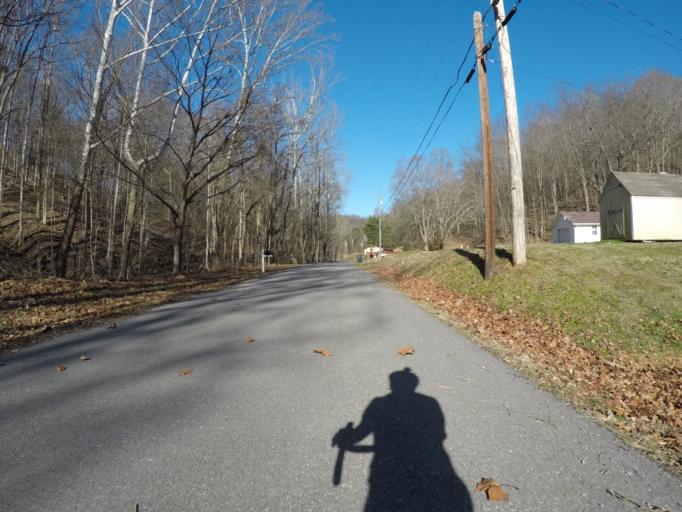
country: US
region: Kentucky
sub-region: Boyd County
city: Catlettsburg
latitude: 38.4138
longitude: -82.6100
